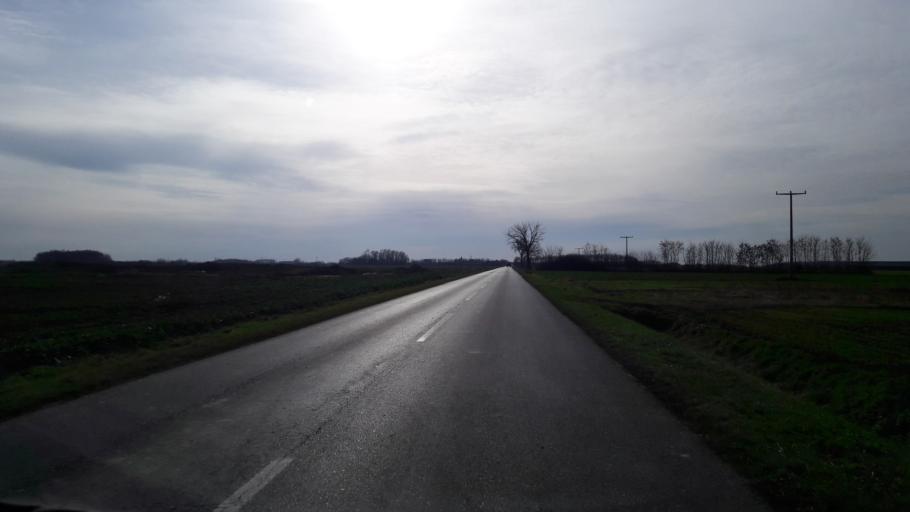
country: HR
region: Osjecko-Baranjska
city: Semeljci
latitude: 45.3237
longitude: 18.5574
